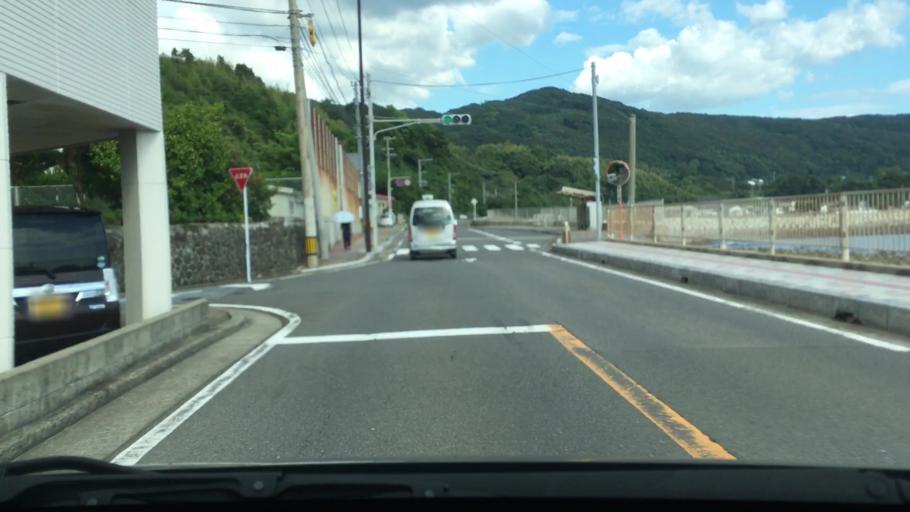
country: JP
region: Nagasaki
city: Togitsu
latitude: 32.8351
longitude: 129.7155
